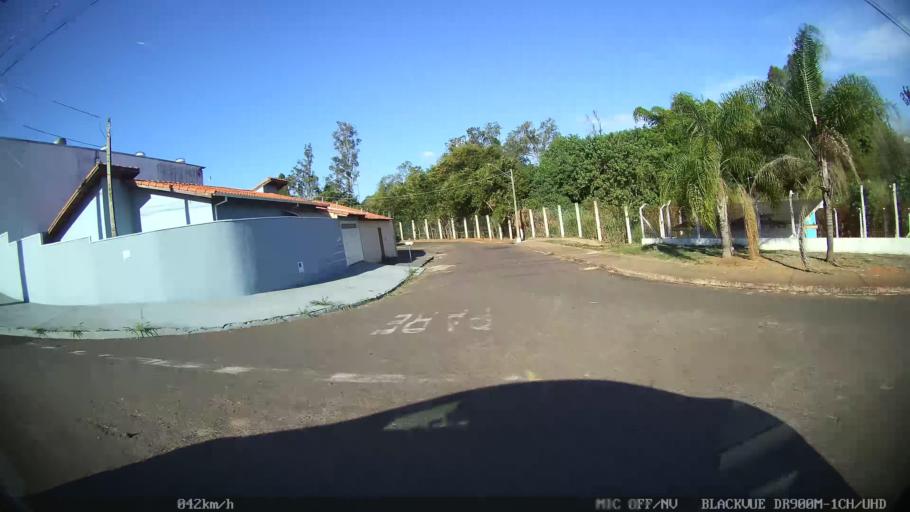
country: BR
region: Sao Paulo
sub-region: Franca
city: Franca
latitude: -20.5103
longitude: -47.4122
